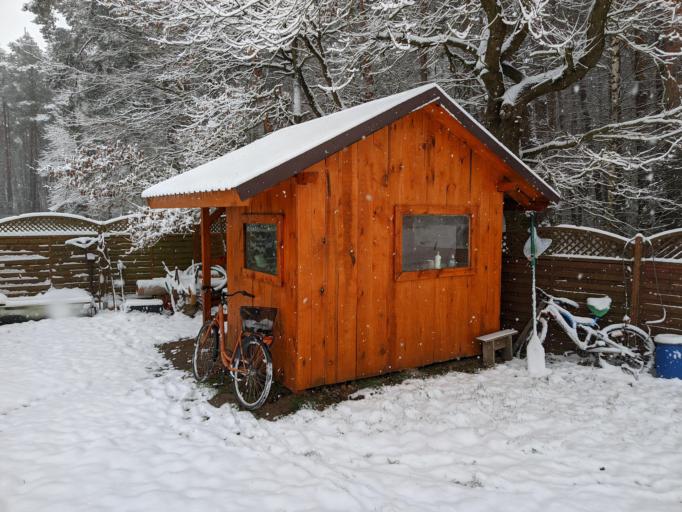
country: PL
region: Lubusz
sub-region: Powiat krosnienski
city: Bobrowice
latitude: 51.9788
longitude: 15.0998
